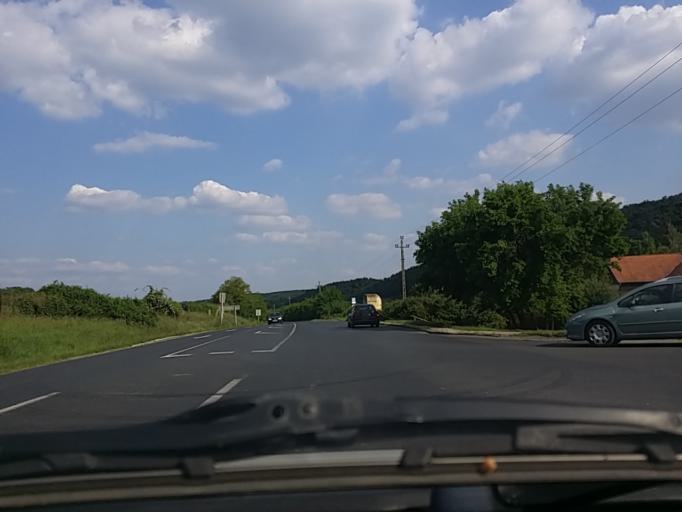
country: HU
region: Pest
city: Csobanka
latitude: 47.6562
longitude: 18.9777
